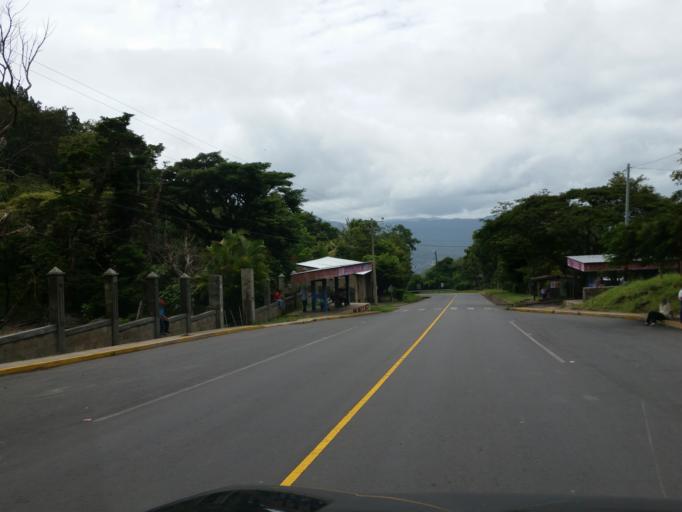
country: NI
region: Matagalpa
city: Matagalpa
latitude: 12.9736
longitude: -85.9205
